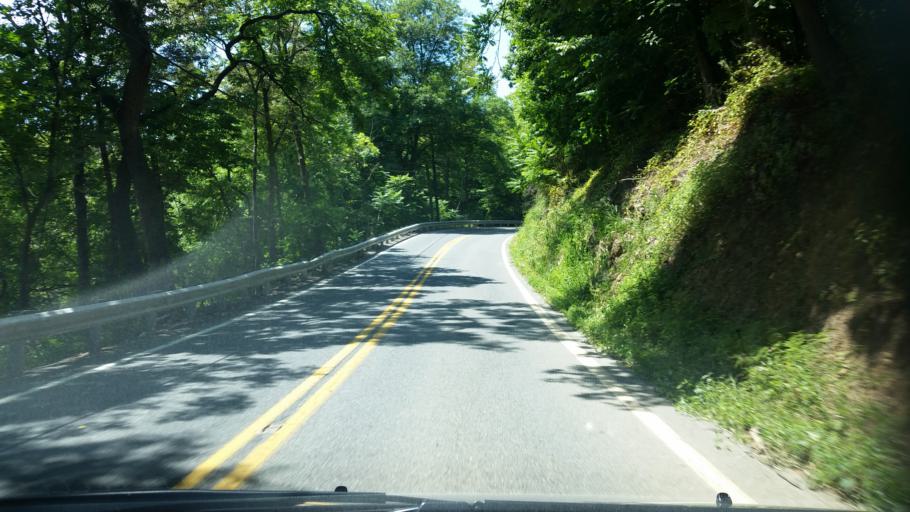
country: US
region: Pennsylvania
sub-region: Dauphin County
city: Hummelstown
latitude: 40.2907
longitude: -76.7005
